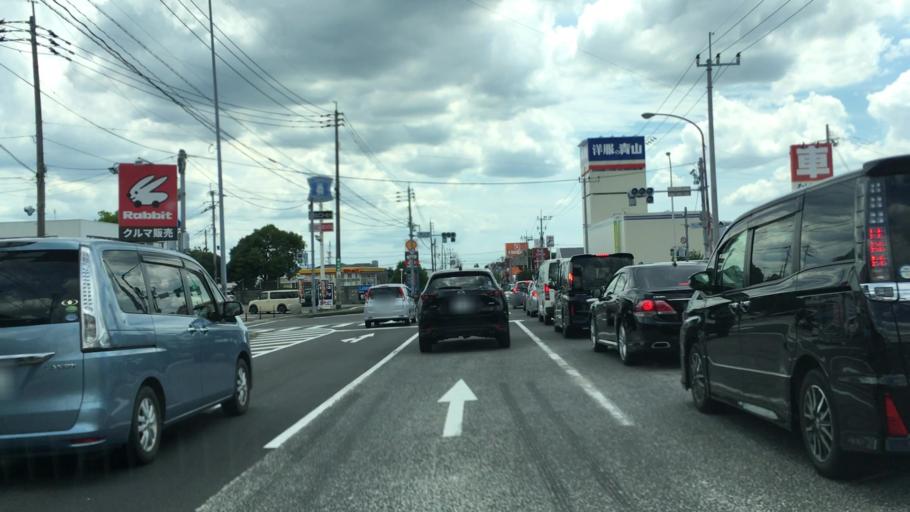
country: JP
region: Saga Prefecture
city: Tosu
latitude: 33.3804
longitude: 130.4991
